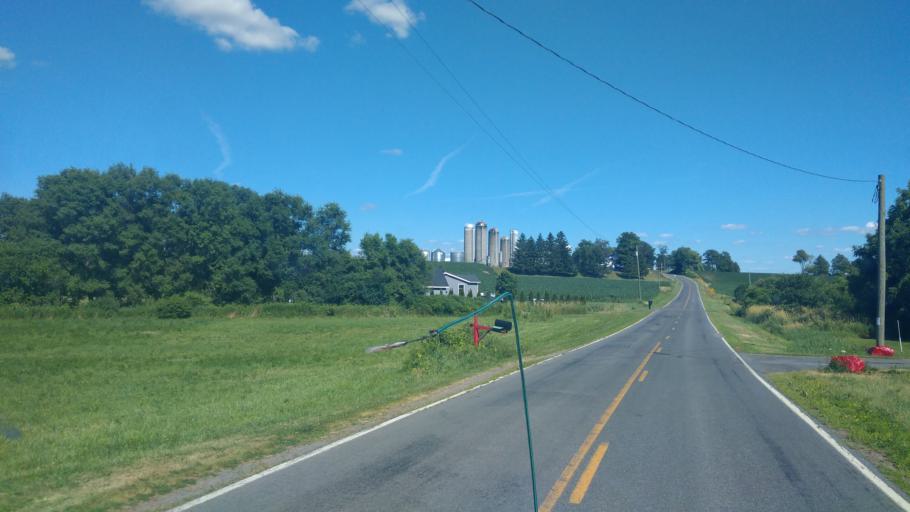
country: US
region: New York
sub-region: Wayne County
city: Clyde
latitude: 43.0221
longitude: -76.8189
